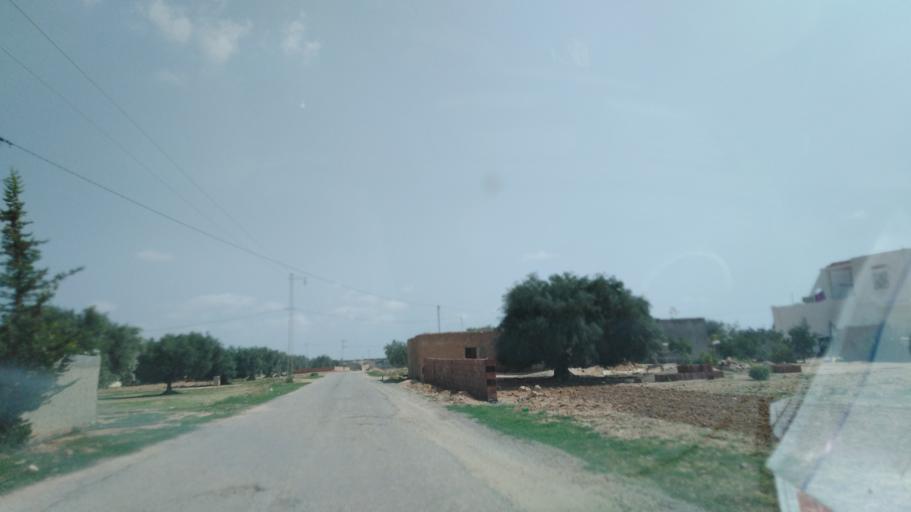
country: TN
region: Safaqis
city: Sfax
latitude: 34.6379
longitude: 10.6126
